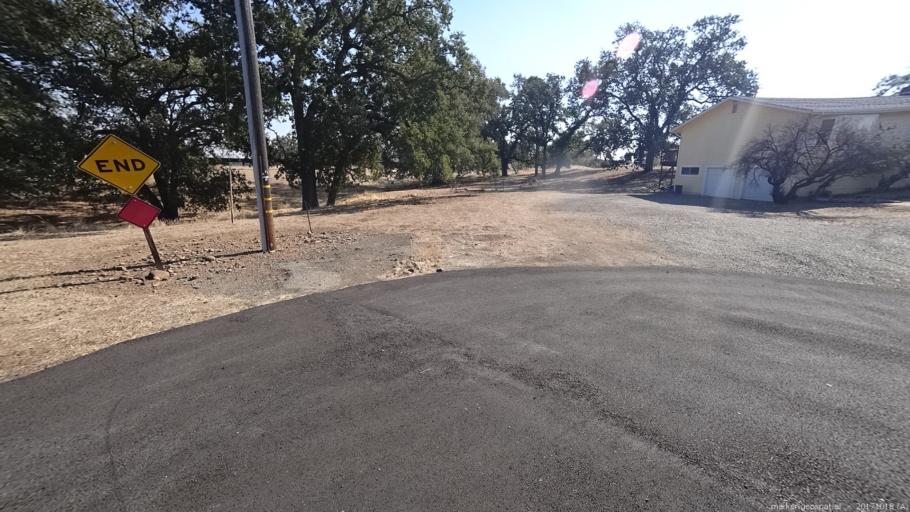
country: US
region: California
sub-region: Shasta County
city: Palo Cedro
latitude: 40.5426
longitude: -122.1784
